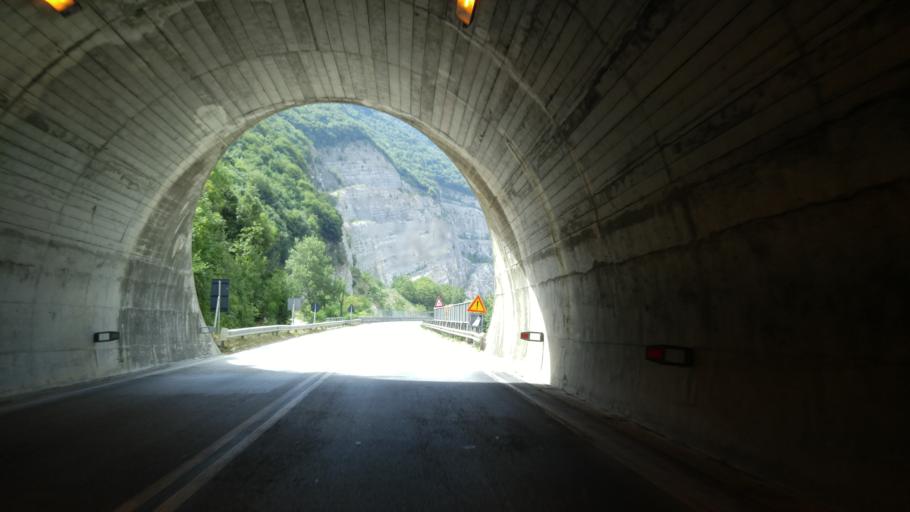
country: IT
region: The Marches
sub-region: Provincia di Pesaro e Urbino
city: Cagli
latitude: 43.5144
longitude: 12.6404
